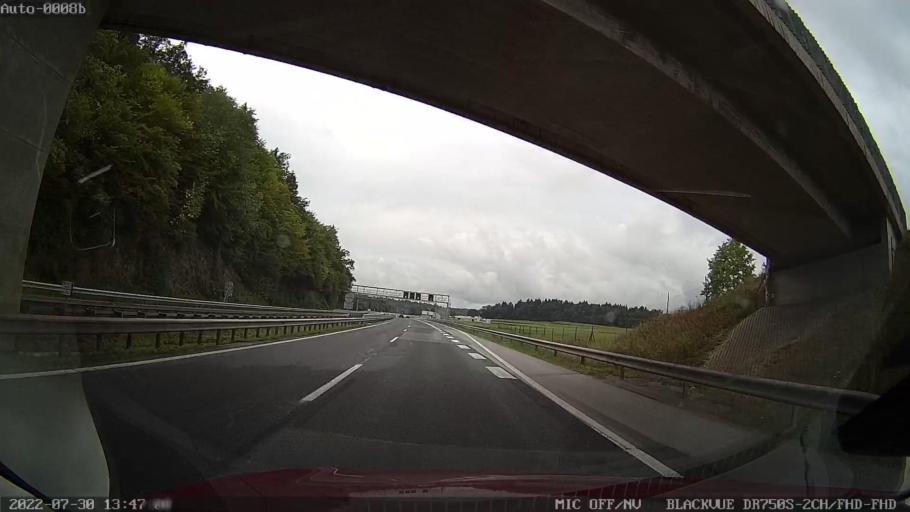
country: SI
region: Ivancna Gorica
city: Sentvid pri Sticni
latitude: 45.9282
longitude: 14.8585
